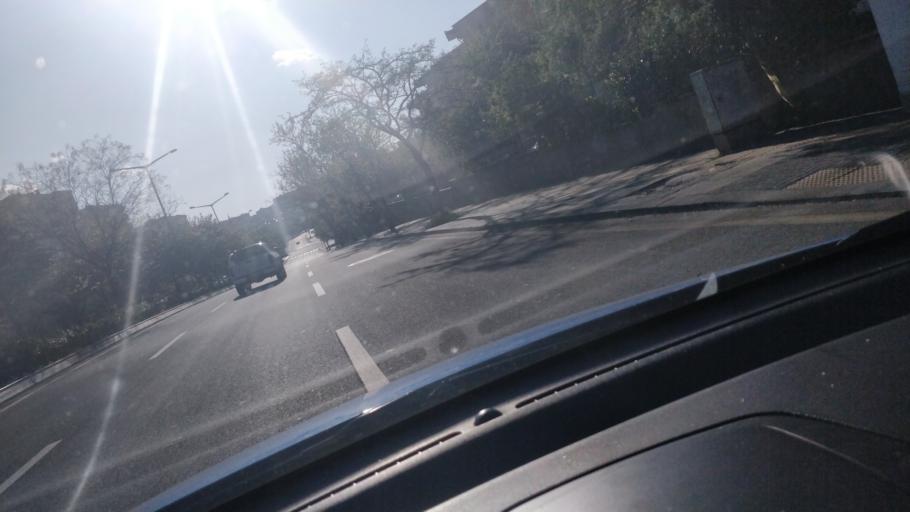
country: TR
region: Ankara
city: Batikent
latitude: 39.9581
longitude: 32.7269
